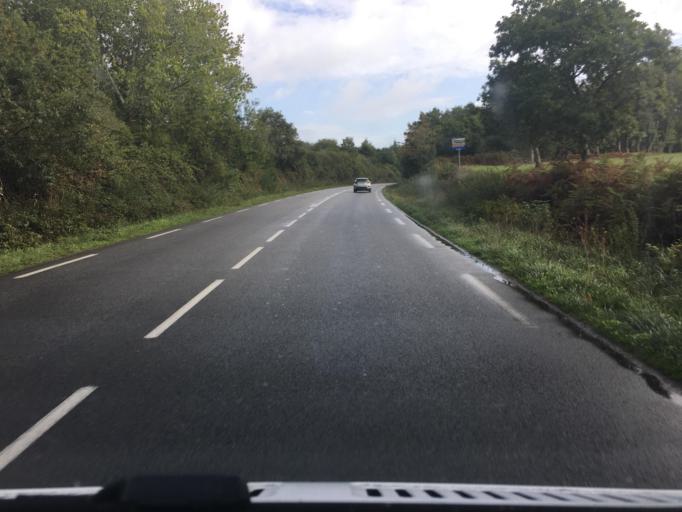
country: FR
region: Brittany
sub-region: Departement du Finistere
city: Ploneour-Lanvern
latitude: 47.8752
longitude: -4.2379
